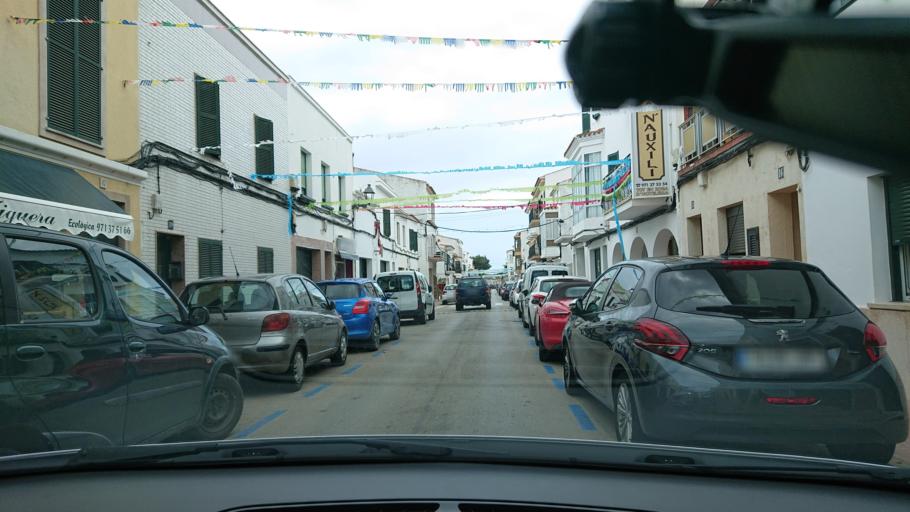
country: ES
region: Balearic Islands
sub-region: Illes Balears
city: Mercadal
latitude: 39.9892
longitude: 4.0936
